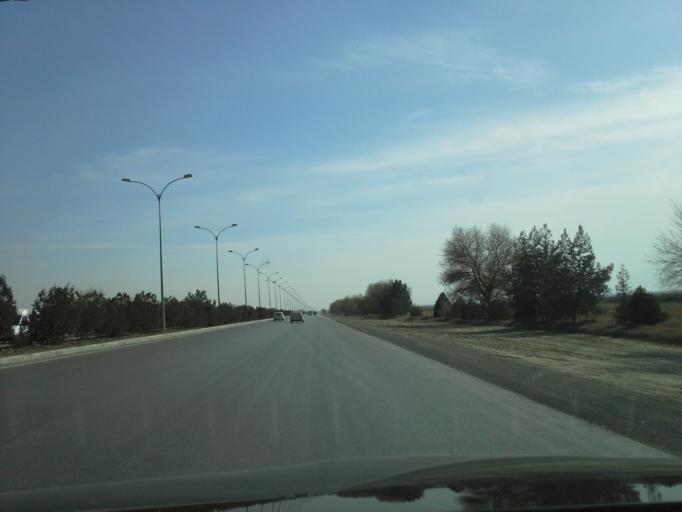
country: TM
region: Ahal
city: Abadan
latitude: 38.1326
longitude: 58.0190
